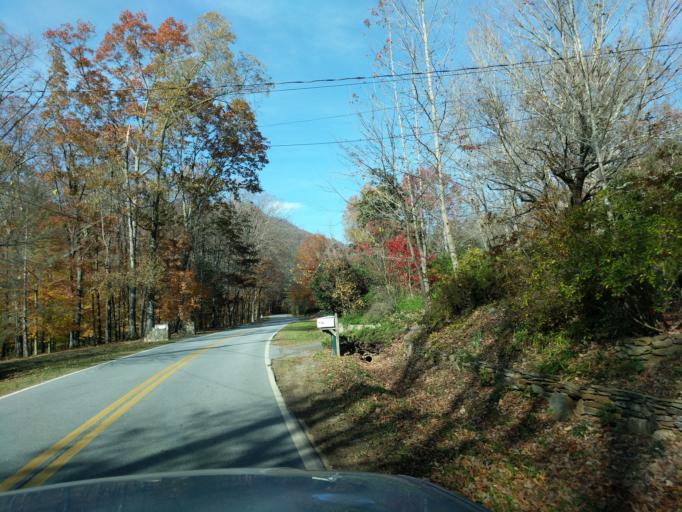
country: US
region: North Carolina
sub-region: Polk County
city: Columbus
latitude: 35.2559
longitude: -82.2068
